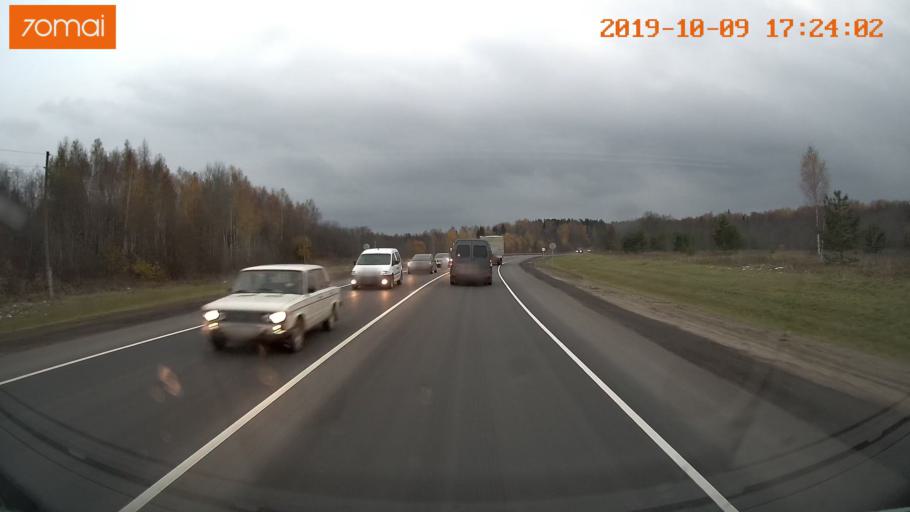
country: RU
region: Ivanovo
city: Furmanov
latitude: 57.1889
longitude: 41.1120
